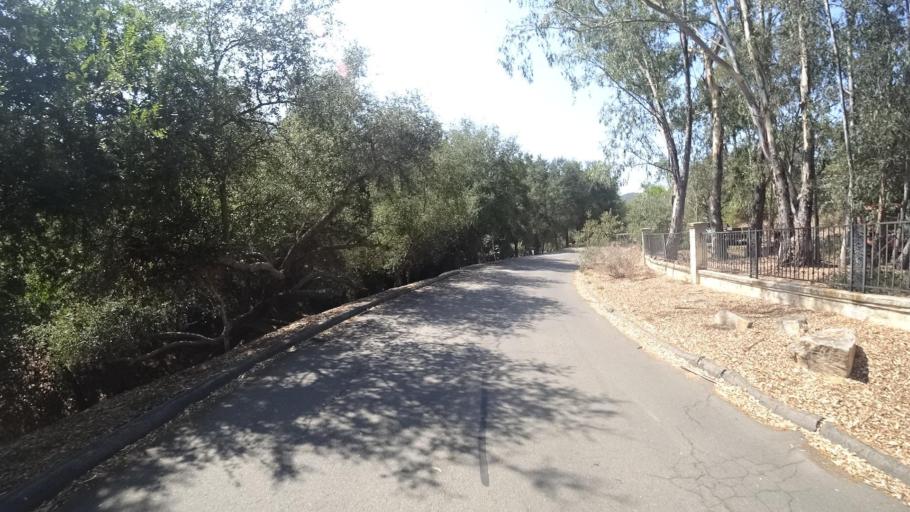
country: US
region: California
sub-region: San Diego County
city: Hidden Meadows
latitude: 33.1822
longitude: -117.1078
